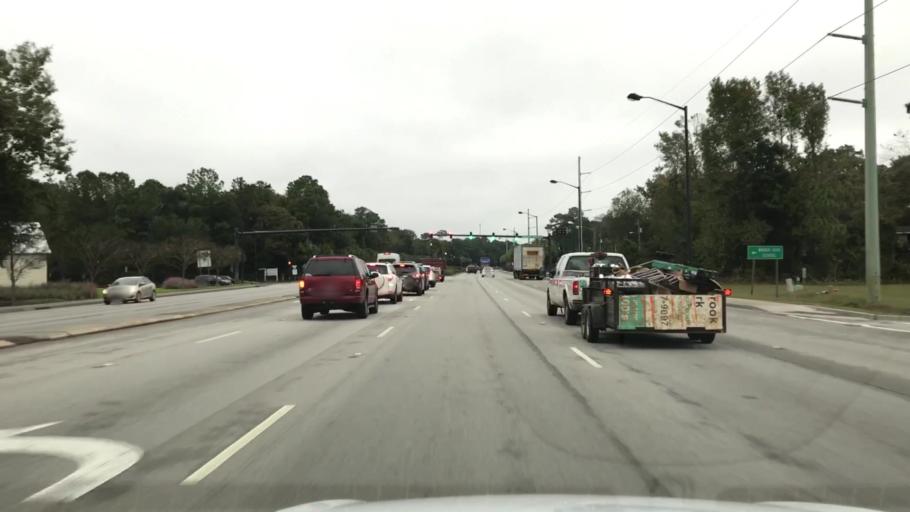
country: US
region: South Carolina
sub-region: Charleston County
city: Isle of Palms
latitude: 32.8802
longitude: -79.7620
